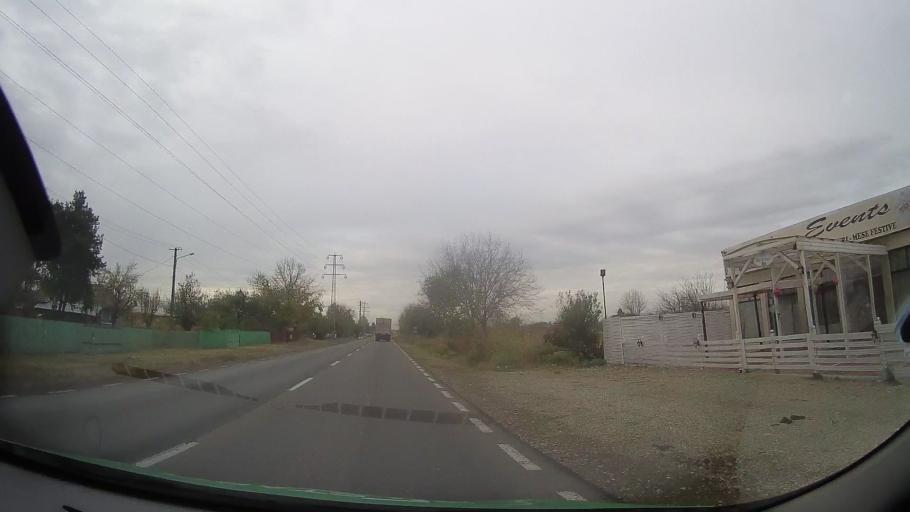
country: RO
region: Prahova
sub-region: Comuna Albesti-Paleologu
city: Albesti-Paleologu
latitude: 44.9550
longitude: 26.2341
